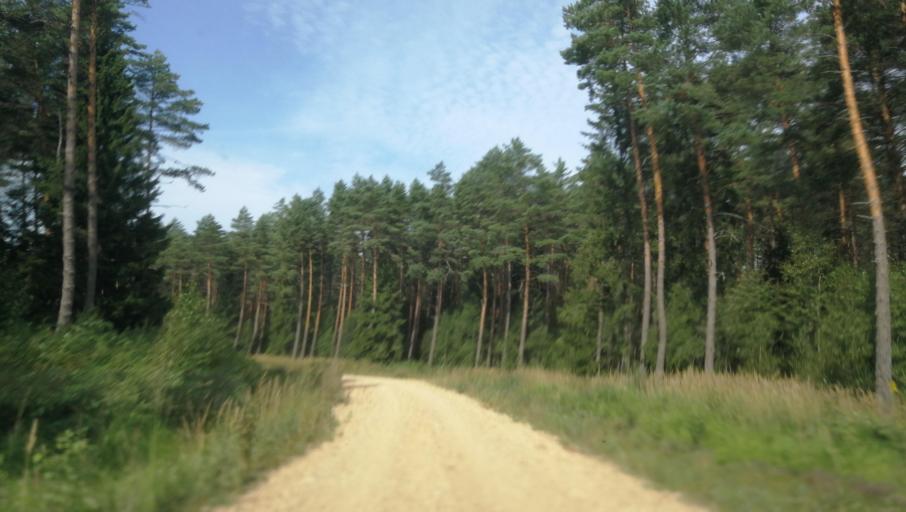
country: LV
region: Pavilostas
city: Pavilosta
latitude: 56.8213
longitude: 21.3221
